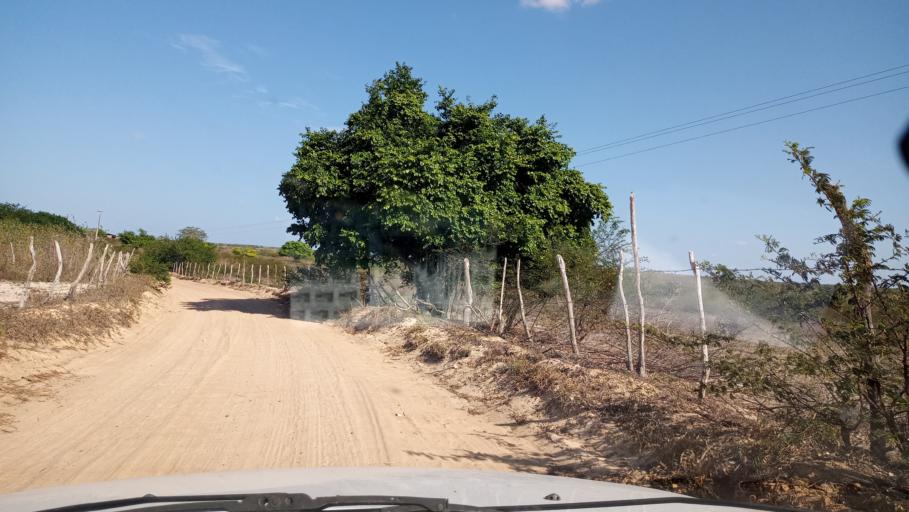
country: BR
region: Rio Grande do Norte
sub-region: Brejinho
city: Brejinho
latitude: -6.1794
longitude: -35.4527
